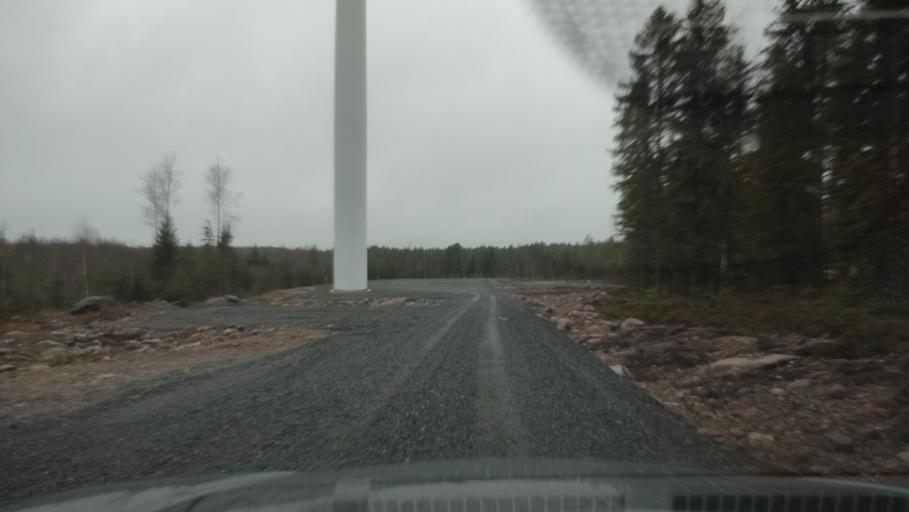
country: FI
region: Southern Ostrobothnia
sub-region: Suupohja
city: Karijoki
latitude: 62.1494
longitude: 21.6147
